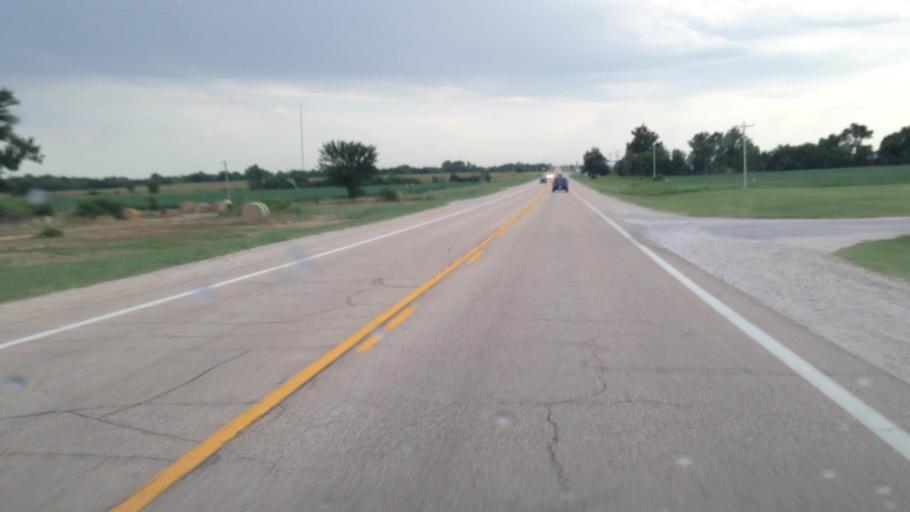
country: US
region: Kansas
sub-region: Coffey County
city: Burlington
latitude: 38.1771
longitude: -95.7388
